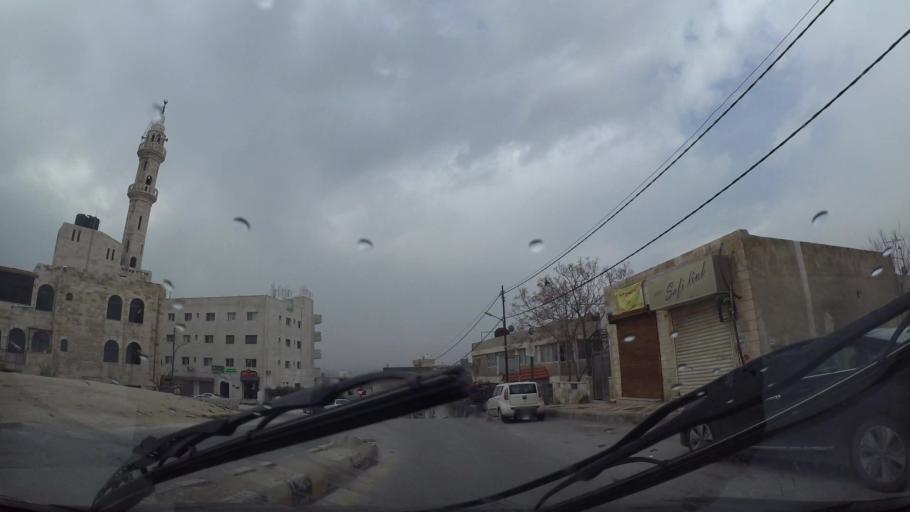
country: JO
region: Amman
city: Amman
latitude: 31.9640
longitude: 35.9364
